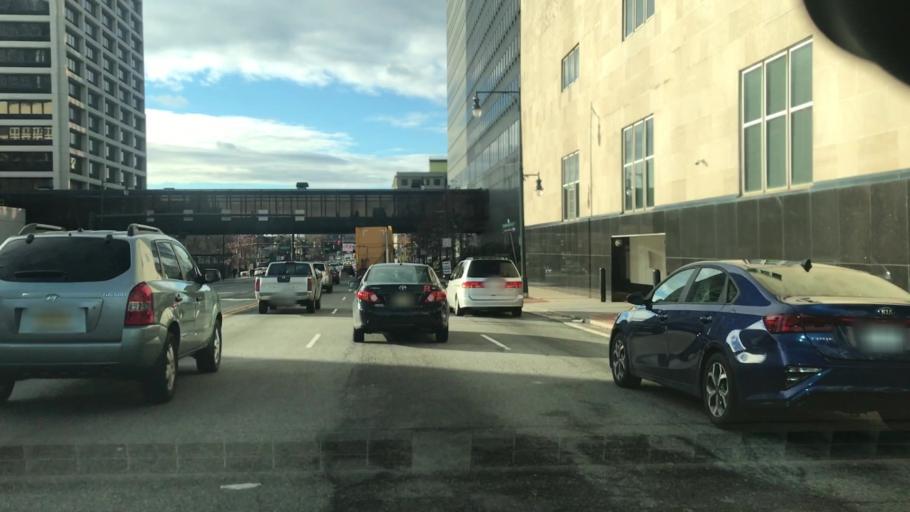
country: US
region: New Jersey
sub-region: Essex County
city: Newark
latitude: 40.7358
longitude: -74.1660
